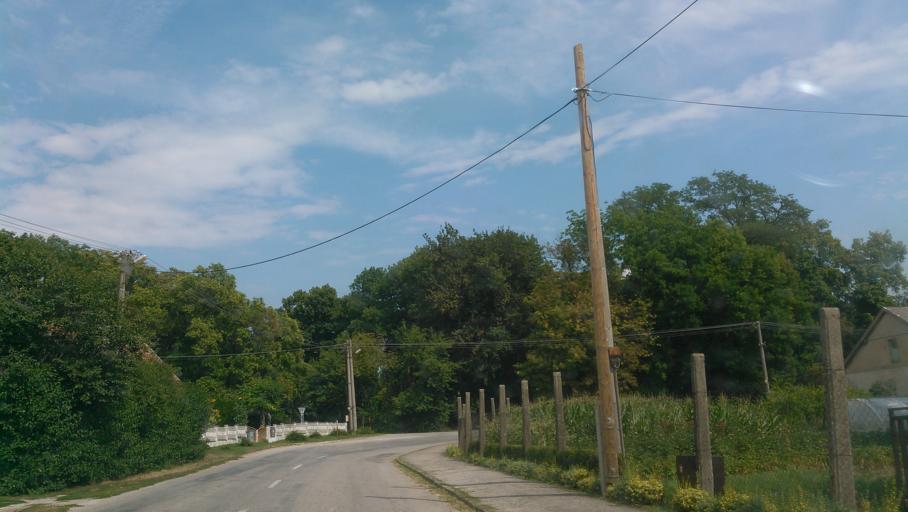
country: SK
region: Nitriansky
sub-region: Okres Nitra
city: Nitra
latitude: 48.4963
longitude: 18.0463
